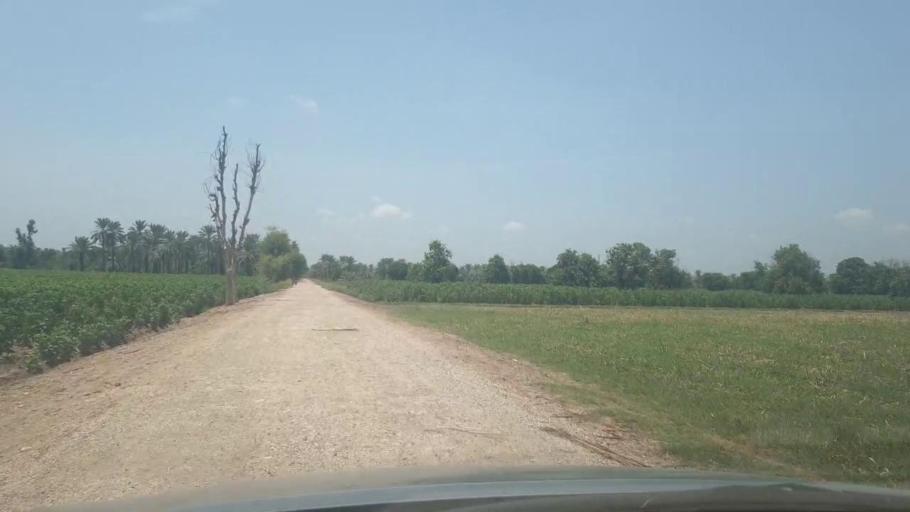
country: PK
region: Sindh
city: Kot Diji
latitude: 27.3887
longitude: 68.6906
